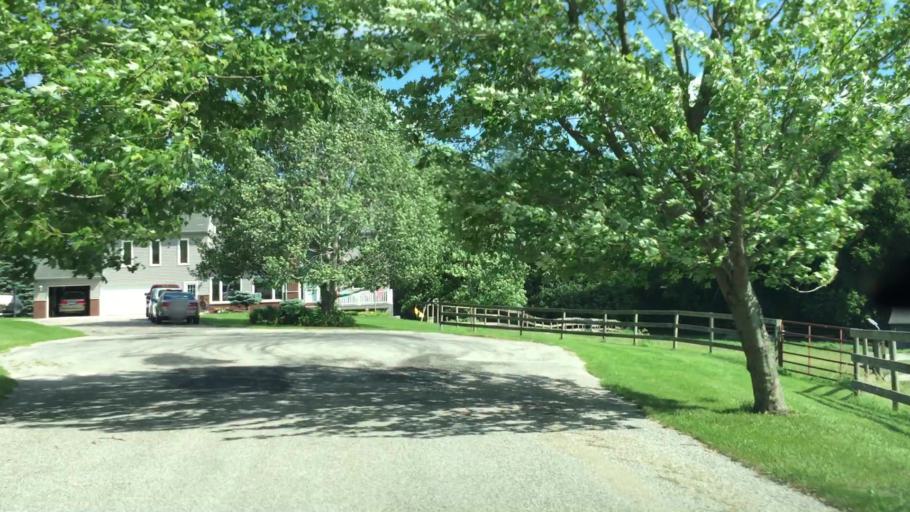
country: US
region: Iowa
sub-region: Johnson County
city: North Liberty
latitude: 41.8013
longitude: -91.6220
